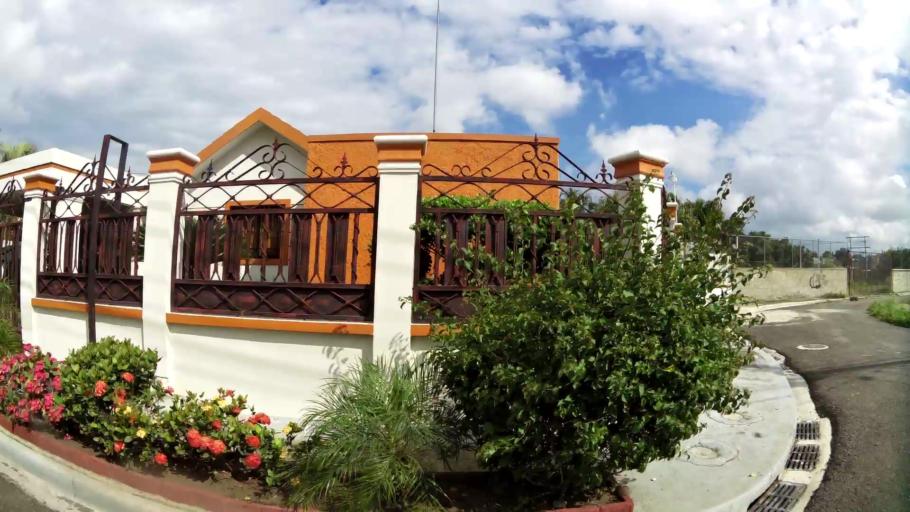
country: DO
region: Santiago
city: Santiago de los Caballeros
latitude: 19.4420
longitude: -70.7051
